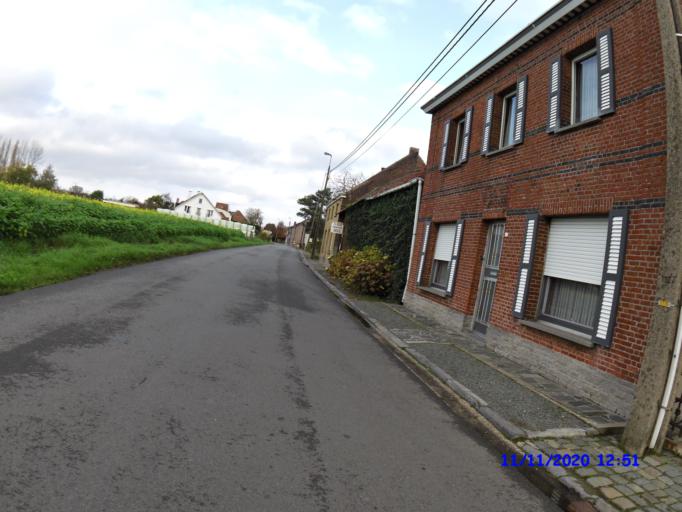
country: BE
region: Flanders
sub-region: Provincie Oost-Vlaanderen
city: Dendermonde
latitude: 51.0166
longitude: 4.0552
